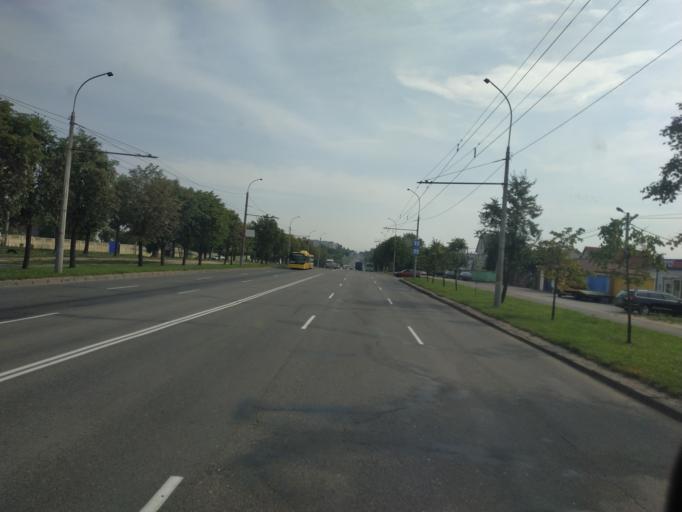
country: BY
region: Mogilev
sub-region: Mahilyowski Rayon
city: Veyno
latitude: 53.8677
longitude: 30.3642
